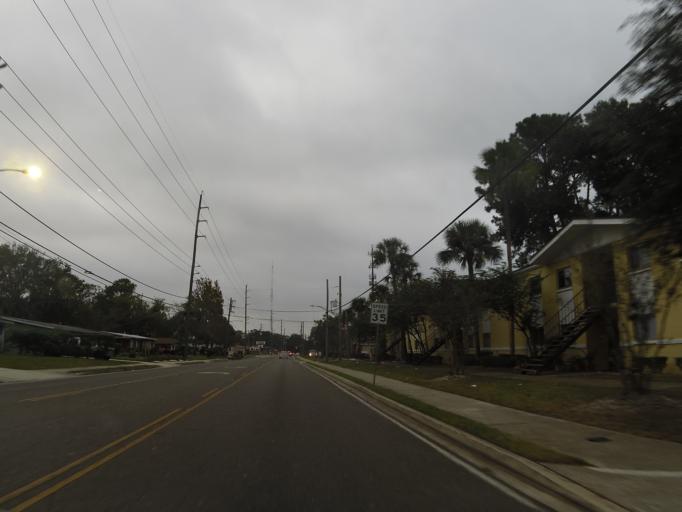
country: US
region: Florida
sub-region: Clay County
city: Bellair-Meadowbrook Terrace
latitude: 30.2794
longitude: -81.7478
